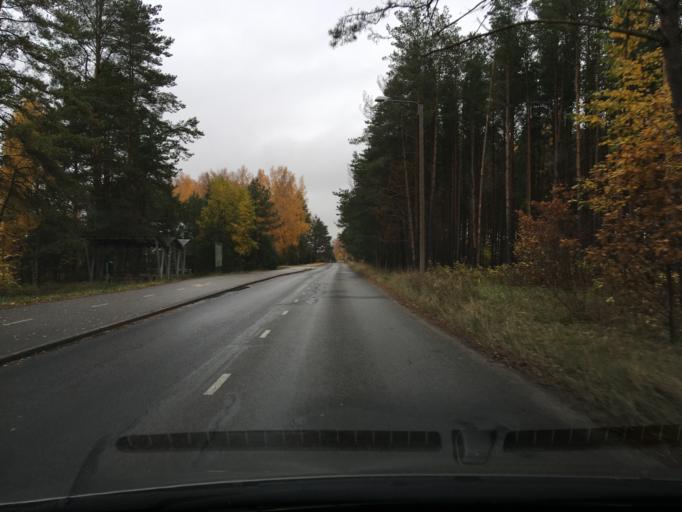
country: EE
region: Tartu
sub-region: Tartu linn
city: Tartu
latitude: 58.3497
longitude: 26.7683
